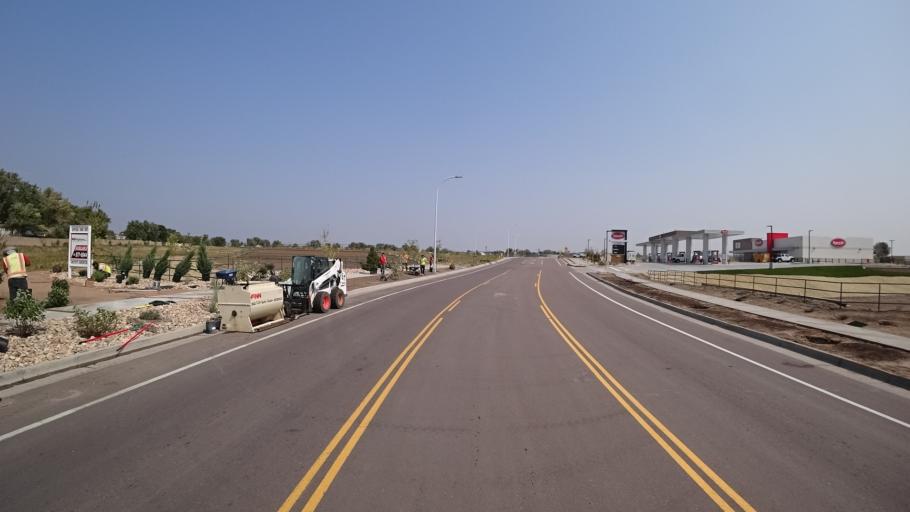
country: US
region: Colorado
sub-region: El Paso County
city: Cimarron Hills
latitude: 38.8259
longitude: -104.7288
